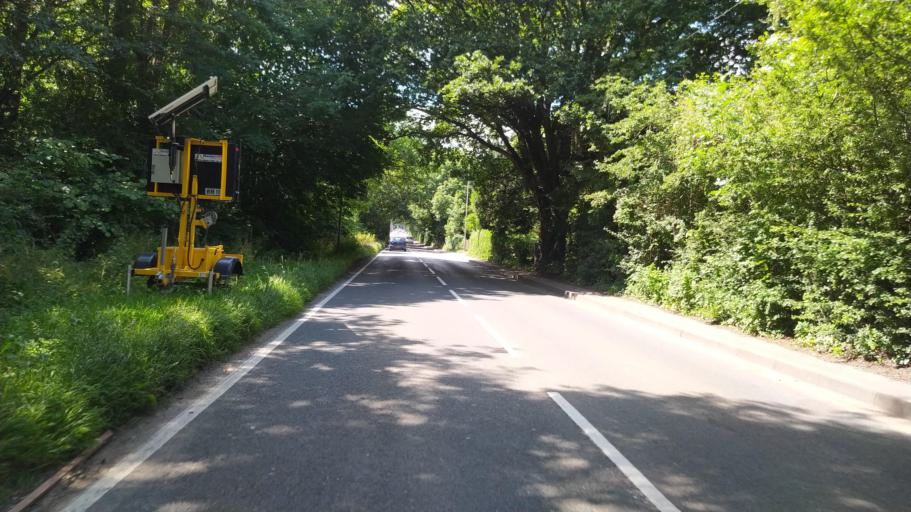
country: GB
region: England
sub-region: Hampshire
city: Netley
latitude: 50.8921
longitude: -1.3407
